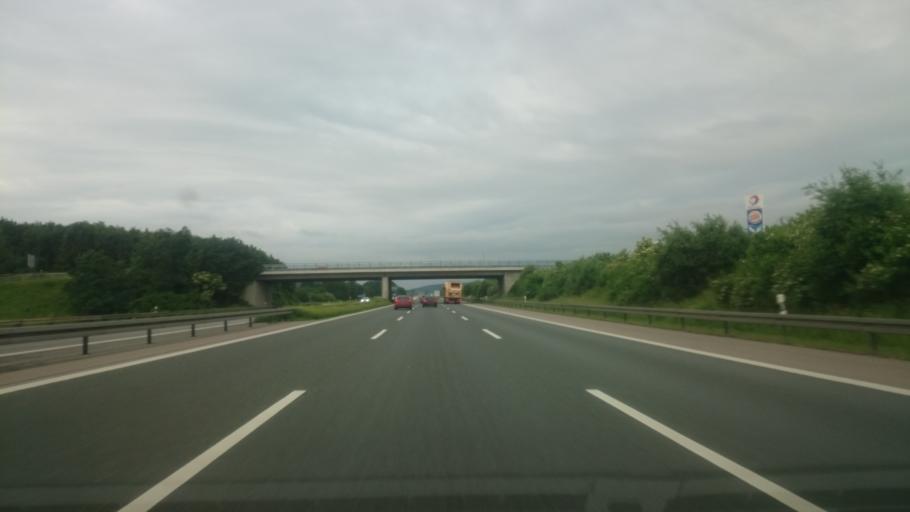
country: DE
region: Bavaria
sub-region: Upper Palatinate
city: Freystadt
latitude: 49.1643
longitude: 11.2633
